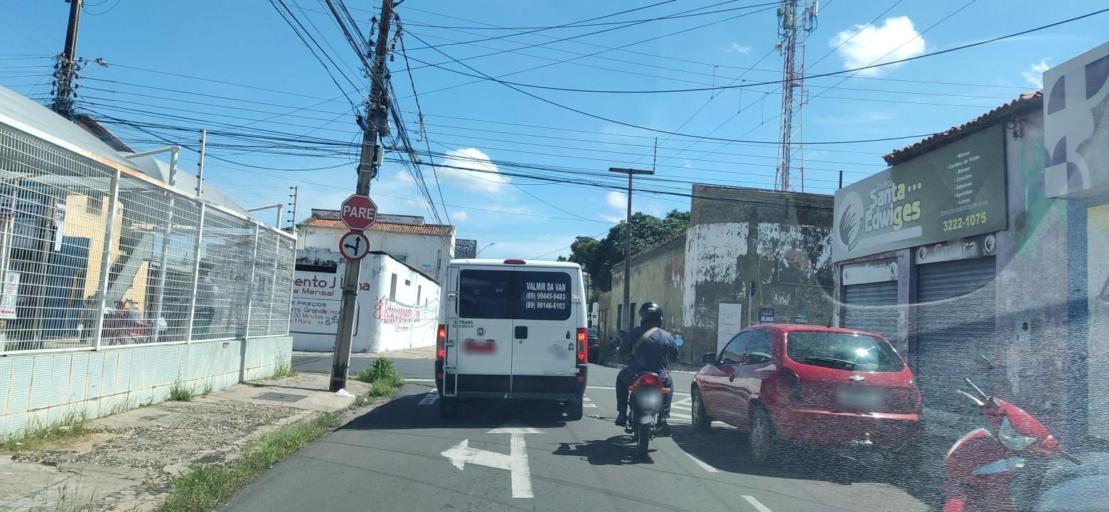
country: BR
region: Piaui
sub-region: Teresina
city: Teresina
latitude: -5.0877
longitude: -42.8146
